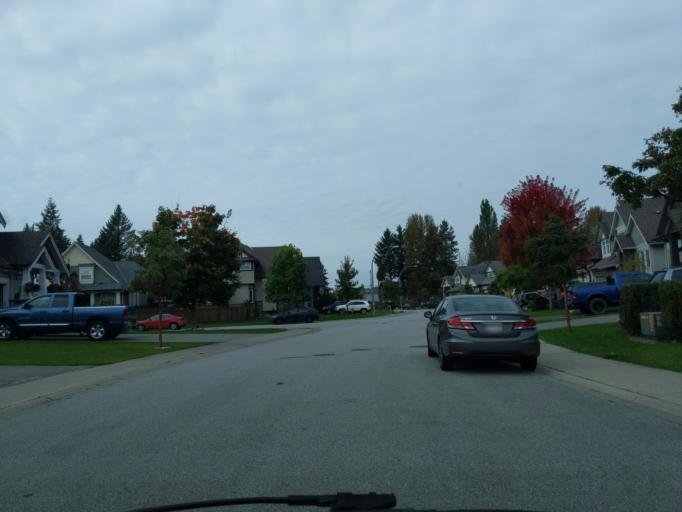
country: CA
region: British Columbia
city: Walnut Grove
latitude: 49.1826
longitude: -122.6582
